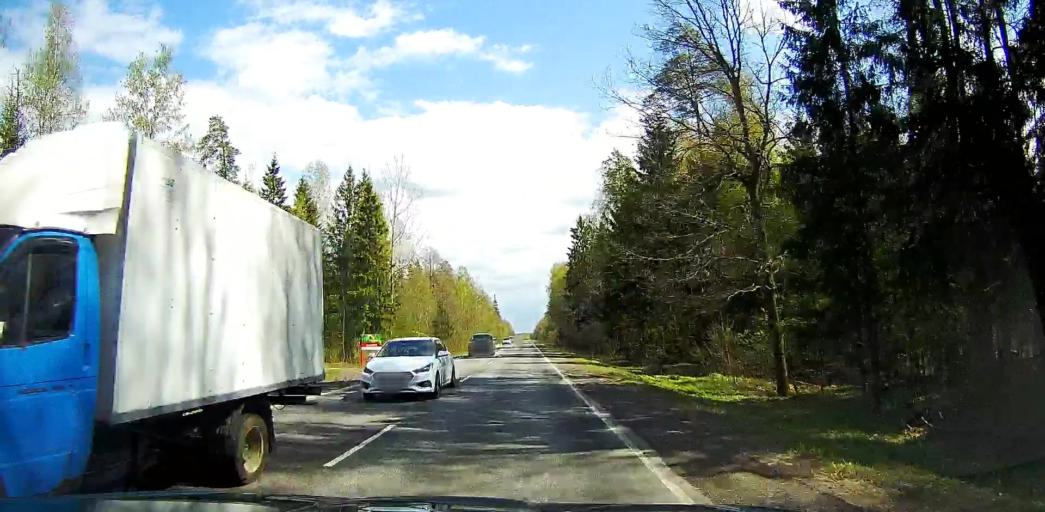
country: RU
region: Moskovskaya
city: Davydovo
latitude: 55.5514
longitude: 38.7771
